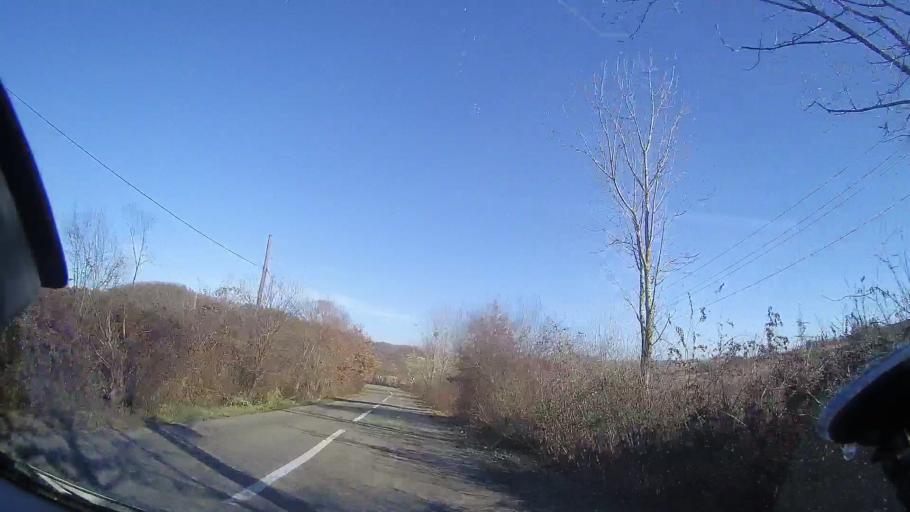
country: RO
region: Bihor
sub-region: Comuna Suncuius
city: Balnaca
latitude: 46.9629
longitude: 22.5514
